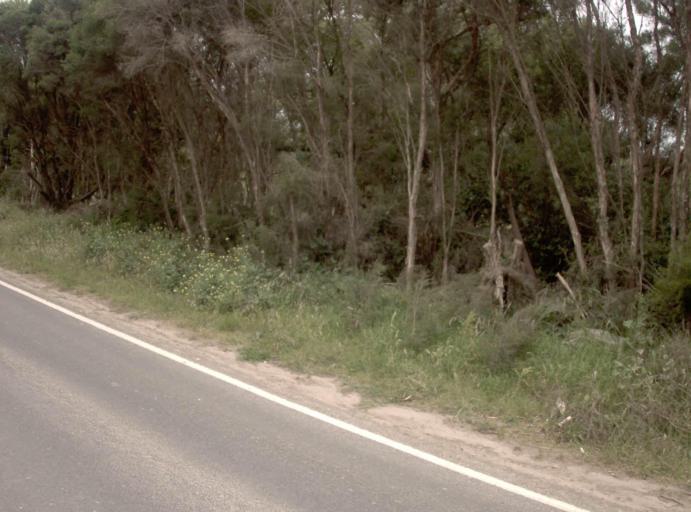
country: AU
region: Victoria
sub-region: Casey
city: Lynbrook
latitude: -38.0557
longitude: 145.2631
